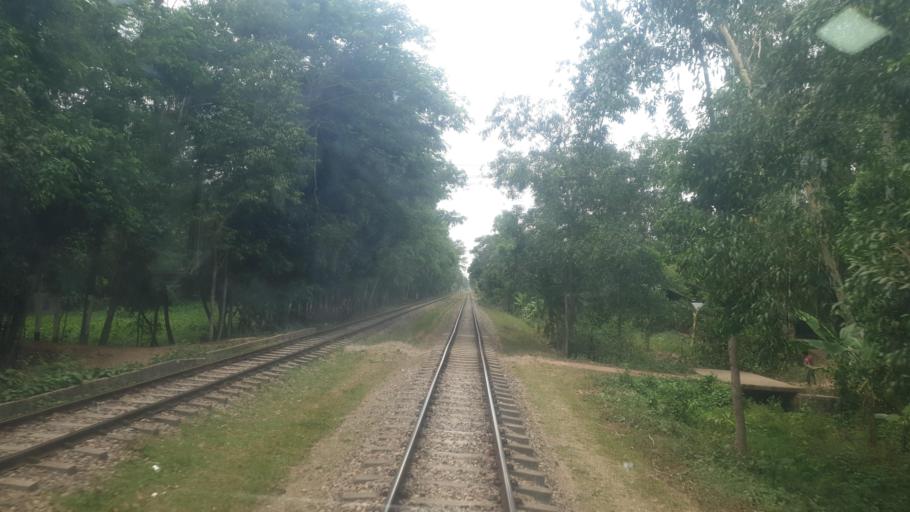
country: BD
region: Chittagong
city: Fatikchari
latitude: 22.6464
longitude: 91.6494
